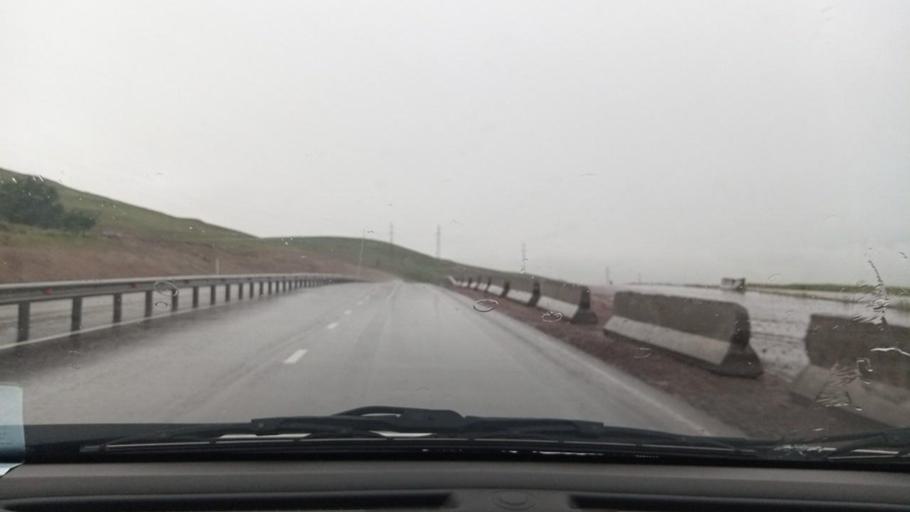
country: UZ
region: Toshkent
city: Angren
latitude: 41.0603
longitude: 70.1760
